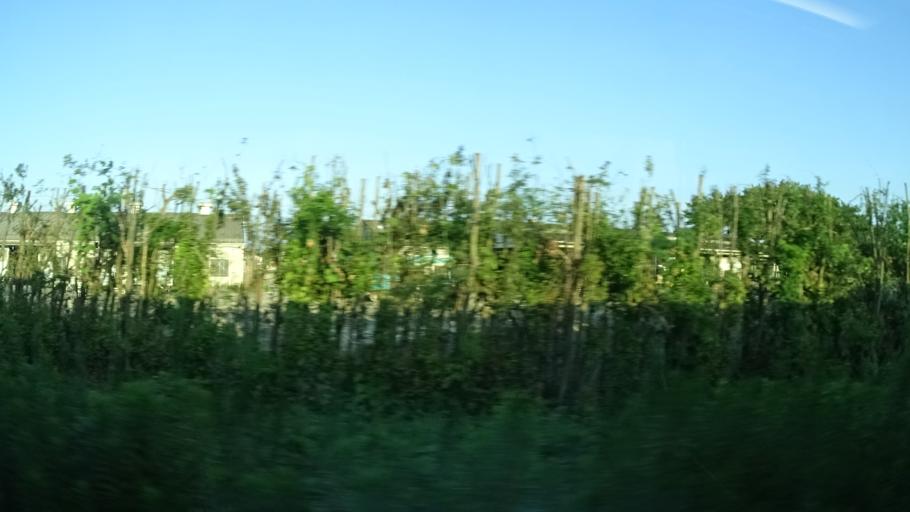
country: JP
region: Ibaraki
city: Ishioka
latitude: 36.1270
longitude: 140.2562
